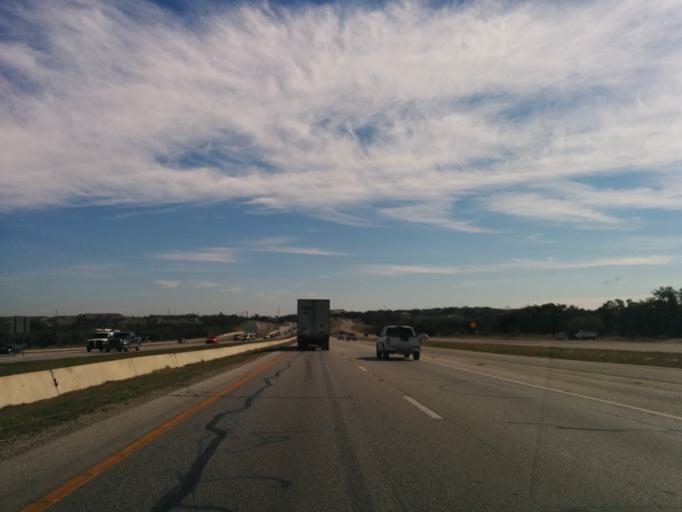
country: US
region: Texas
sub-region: Bexar County
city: Shavano Park
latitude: 29.6017
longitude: -98.5449
